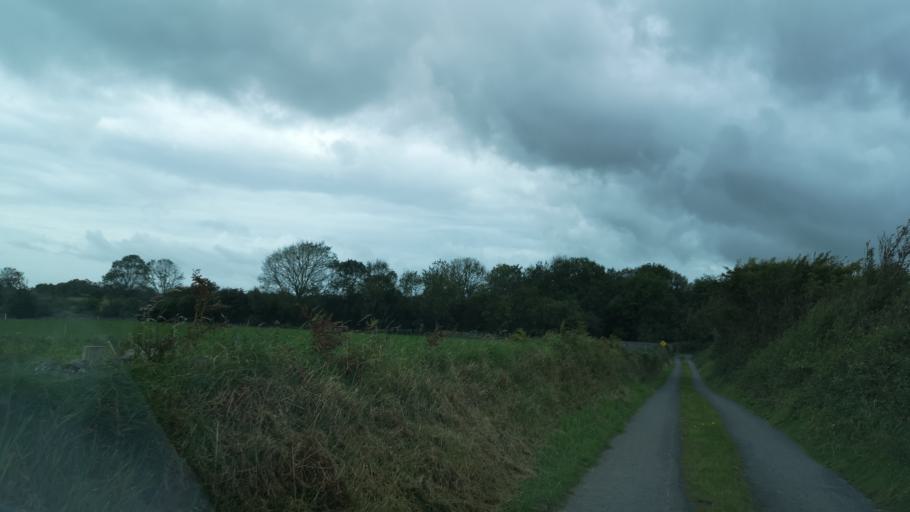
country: IE
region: Connaught
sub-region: County Galway
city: Athenry
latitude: 53.2849
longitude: -8.7142
